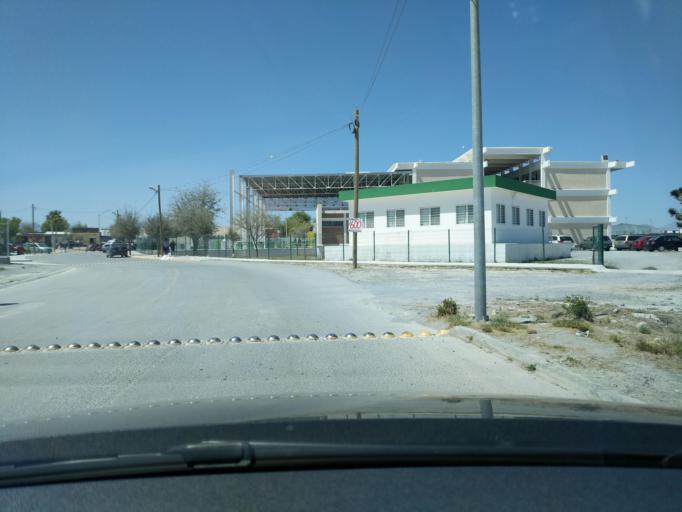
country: MX
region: Nuevo Leon
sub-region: Apodaca
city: Artemio Trevino
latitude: 25.8406
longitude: -100.1409
